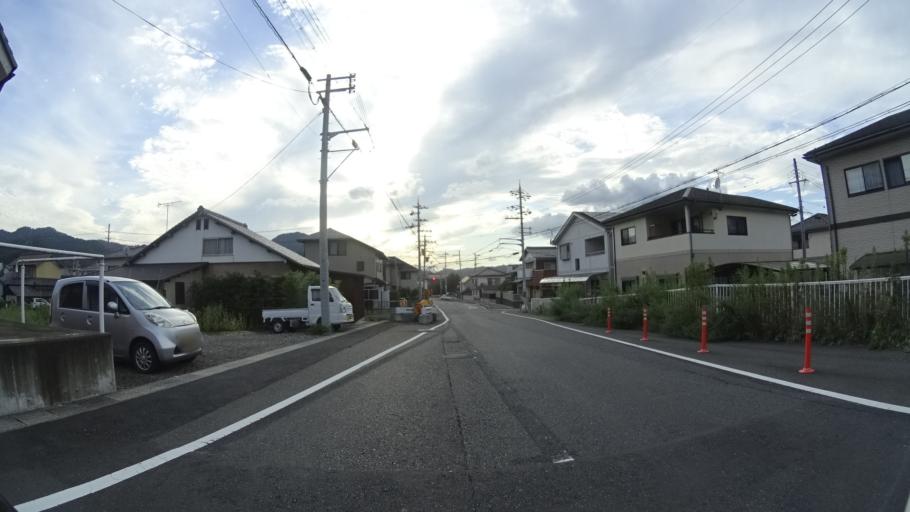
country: JP
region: Kyoto
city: Maizuru
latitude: 35.4266
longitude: 135.3338
